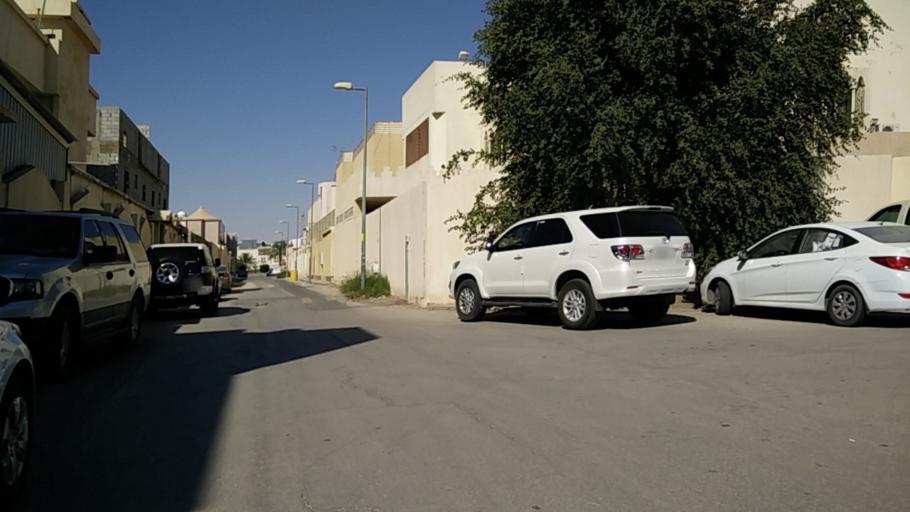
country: SA
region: Ar Riyad
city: Riyadh
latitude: 24.7486
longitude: 46.6704
